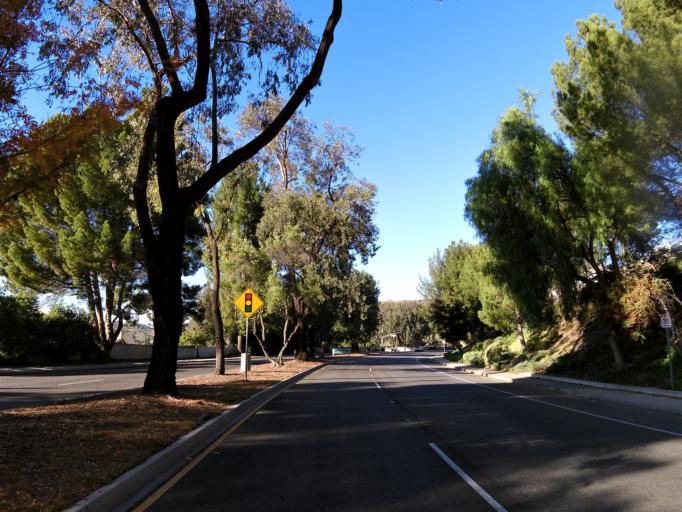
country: US
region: California
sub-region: Ventura County
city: Casa Conejo
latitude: 34.2191
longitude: -118.8896
